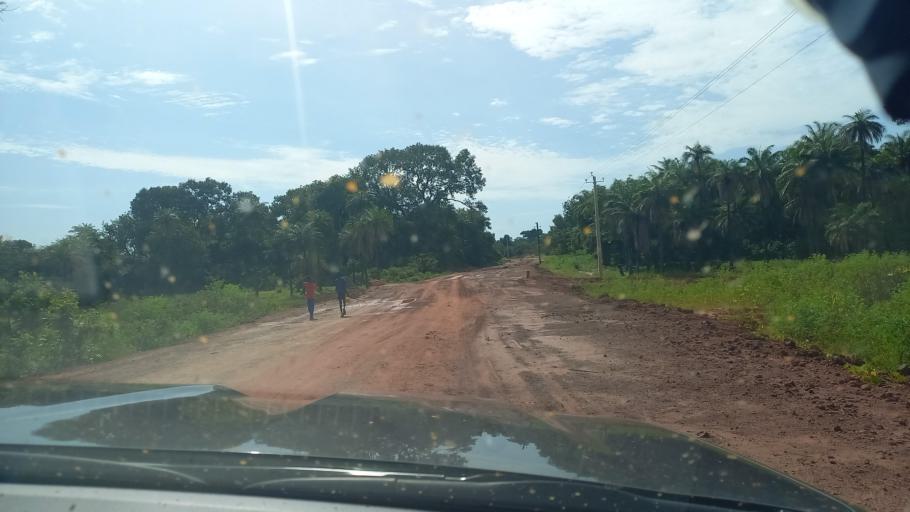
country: SN
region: Ziguinchor
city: Ziguinchor
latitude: 12.6728
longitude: -16.1913
